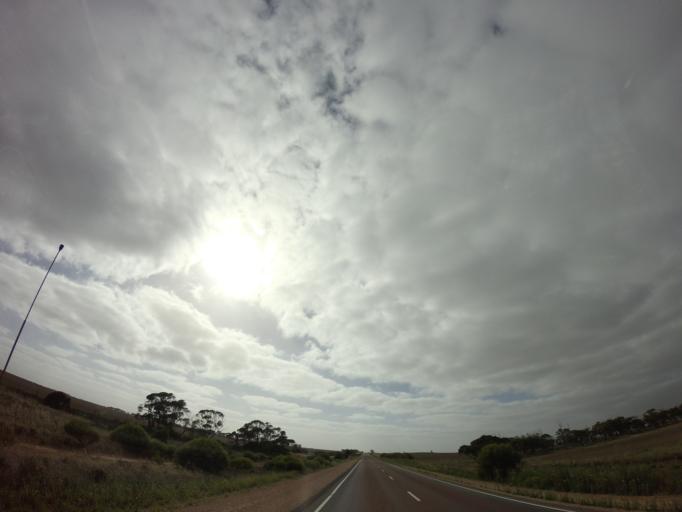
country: AU
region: South Australia
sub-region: Ceduna
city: Ceduna
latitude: -32.2530
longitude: 134.1854
